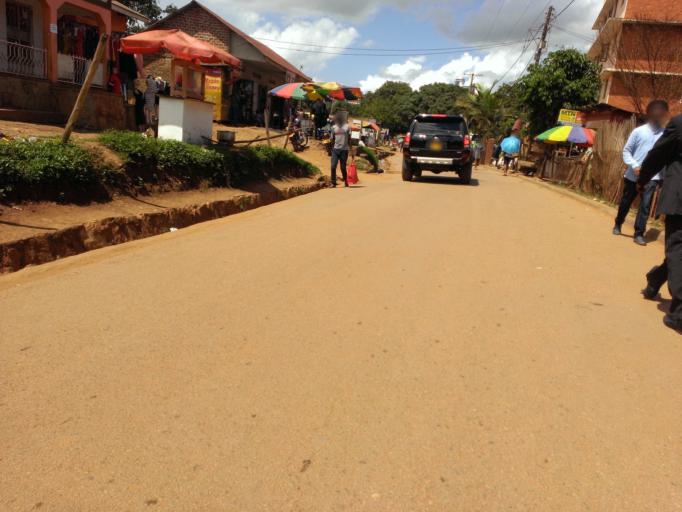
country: UG
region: Central Region
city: Kampala Central Division
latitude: 0.3255
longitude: 32.5670
